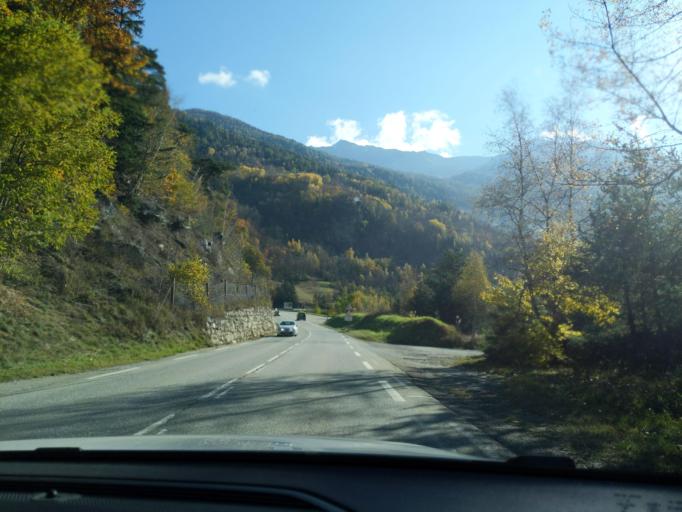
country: FR
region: Rhone-Alpes
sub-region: Departement de la Savoie
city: Seez
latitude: 45.5980
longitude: 6.8755
